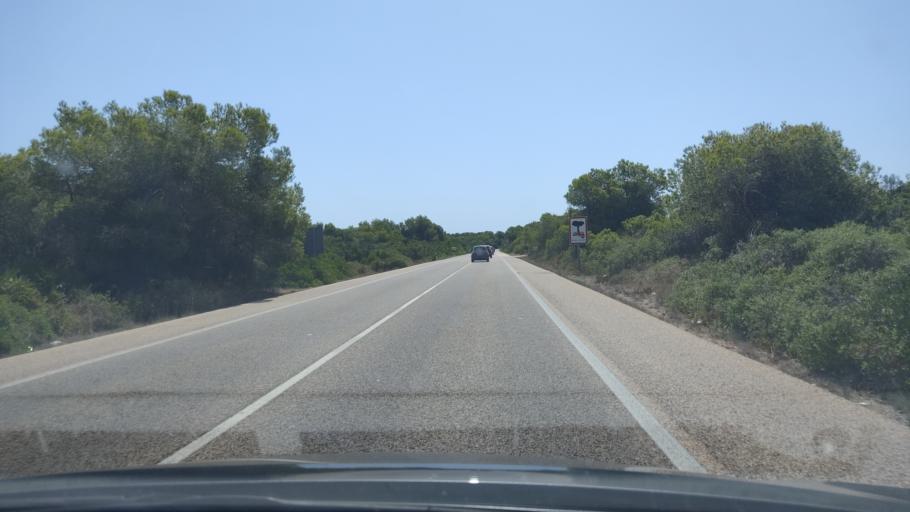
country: ES
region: Valencia
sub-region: Provincia de Valencia
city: Sollana
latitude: 39.3144
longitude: -0.3026
